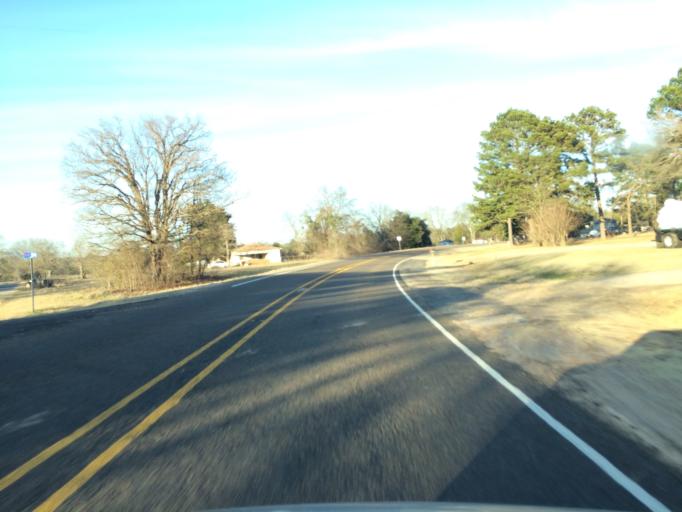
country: US
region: Texas
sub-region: Wood County
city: Hawkins
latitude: 32.6318
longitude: -95.2743
